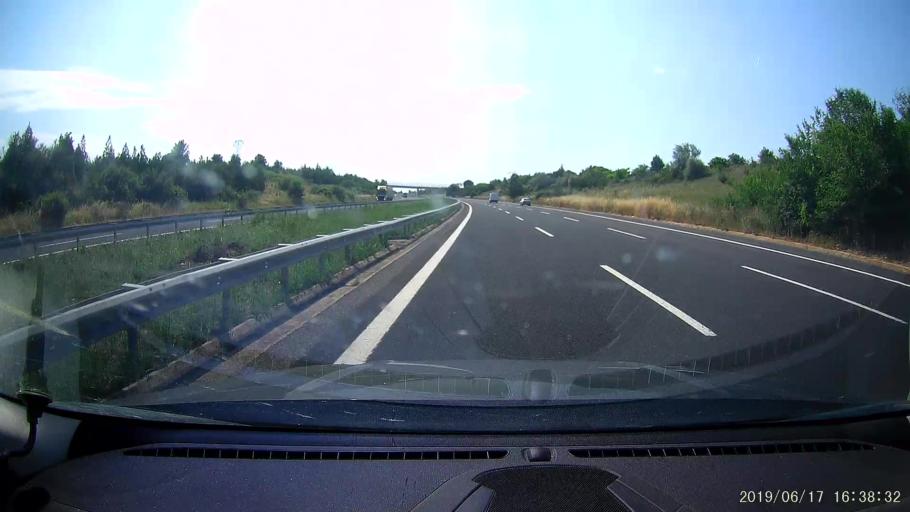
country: TR
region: Kirklareli
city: Luleburgaz
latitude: 41.4467
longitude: 27.4399
